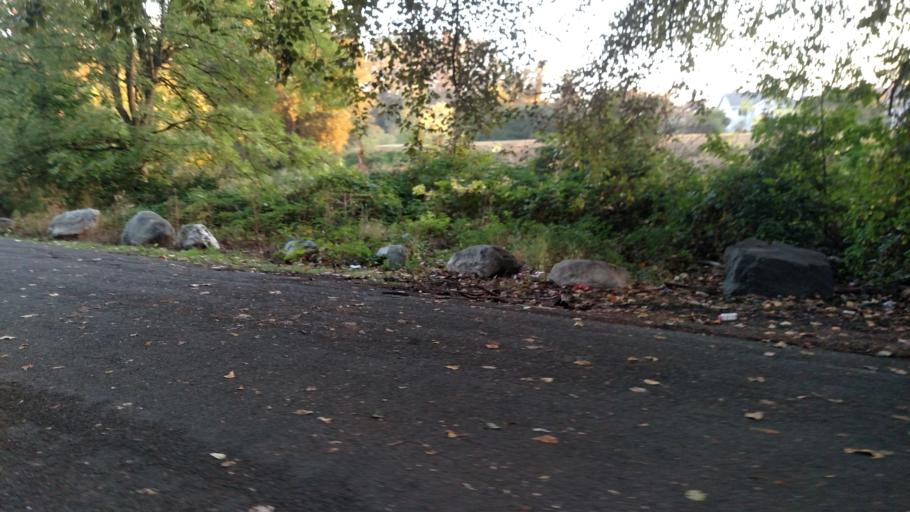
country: US
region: Washington
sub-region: King County
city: Kent
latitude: 47.3879
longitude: -122.2722
